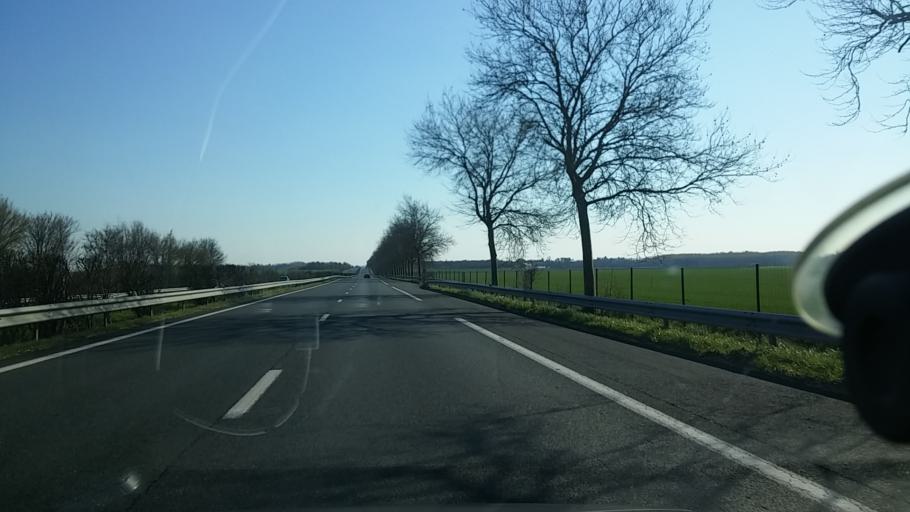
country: FR
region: Centre
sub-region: Departement de l'Indre
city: Montierchaume
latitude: 46.9418
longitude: 1.7511
